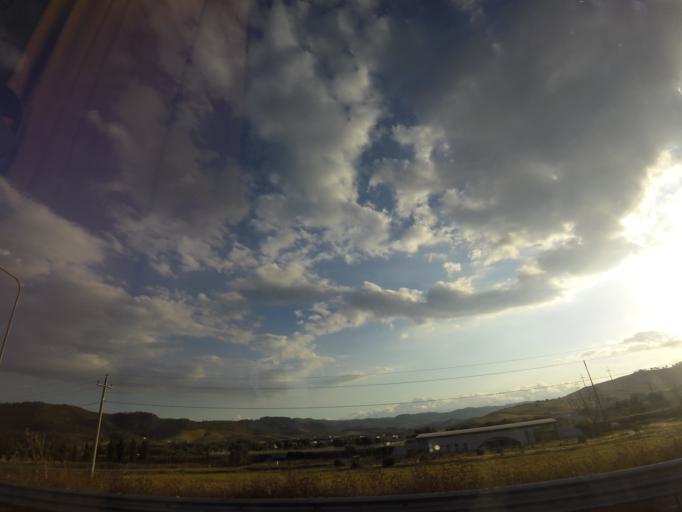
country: IT
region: Calabria
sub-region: Provincia di Catanzaro
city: Catanzaro
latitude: 38.8663
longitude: 16.5651
